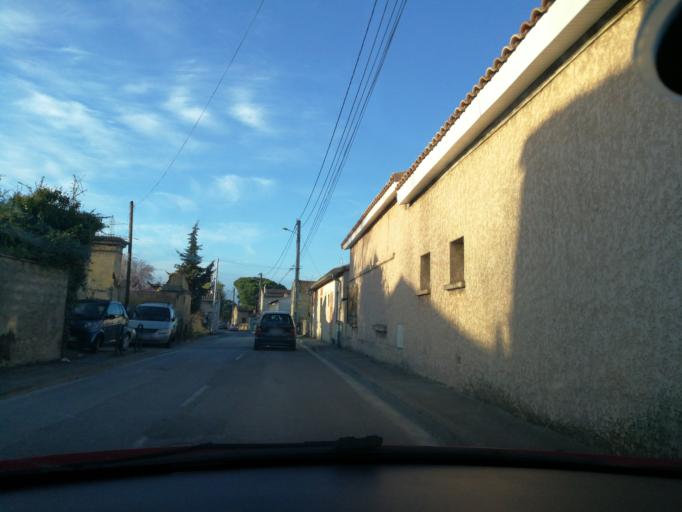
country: FR
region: Midi-Pyrenees
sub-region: Departement de la Haute-Garonne
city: Blagnac
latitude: 43.6460
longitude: 1.4145
